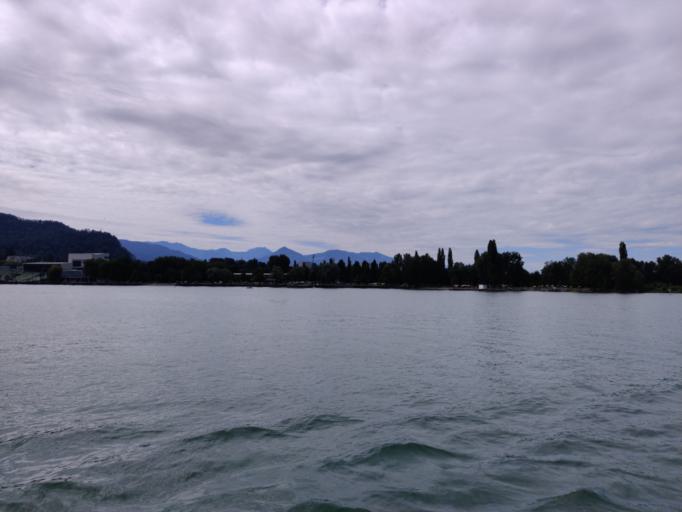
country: AT
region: Vorarlberg
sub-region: Politischer Bezirk Bregenz
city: Bregenz
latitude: 47.5097
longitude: 9.7338
